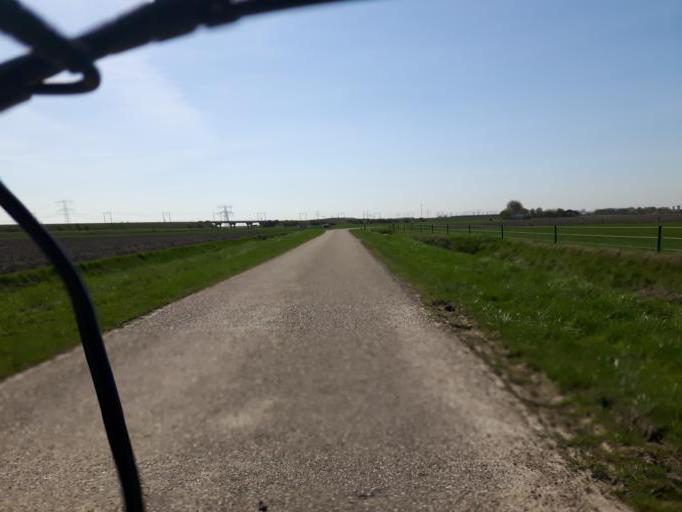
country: NL
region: Zeeland
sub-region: Gemeente Reimerswaal
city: Yerseke
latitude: 51.4734
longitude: 3.9985
